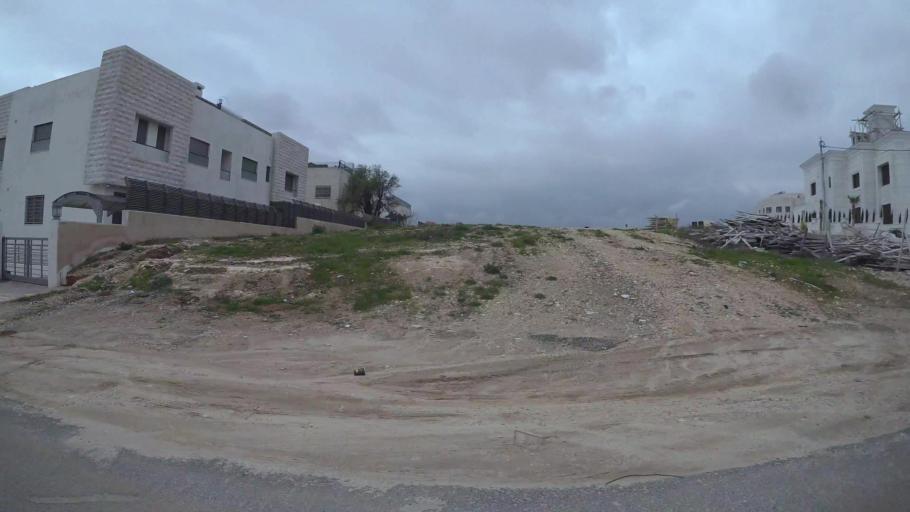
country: JO
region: Amman
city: Wadi as Sir
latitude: 31.9918
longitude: 35.8361
